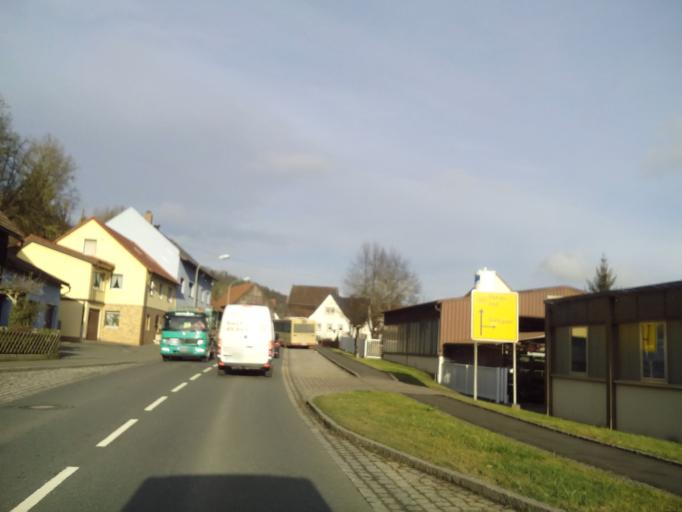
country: DE
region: Bavaria
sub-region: Upper Franconia
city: Untersteinach
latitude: 50.1178
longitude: 11.5034
